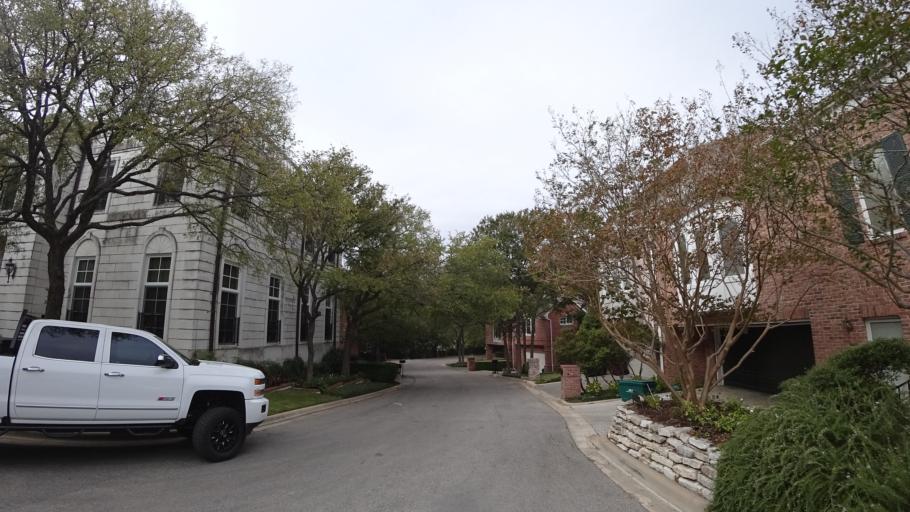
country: US
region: Texas
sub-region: Travis County
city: Rollingwood
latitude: 30.3029
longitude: -97.7659
